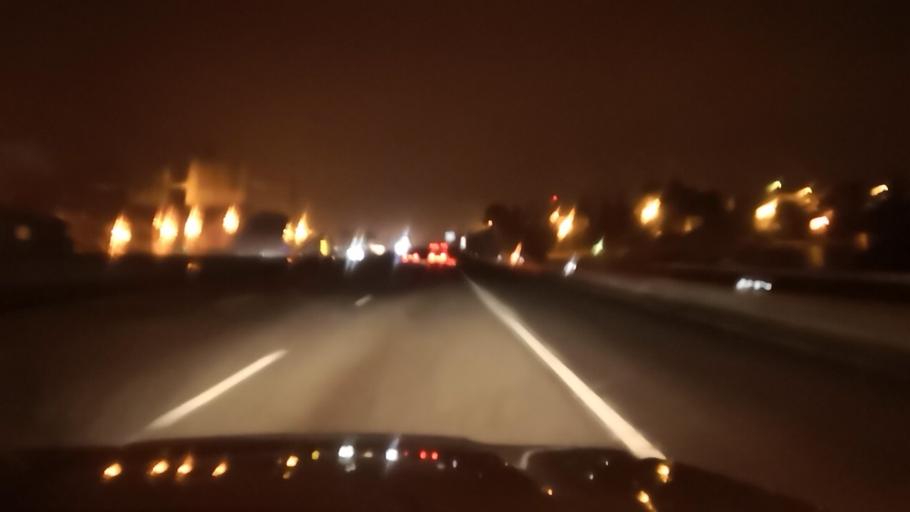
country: PT
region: Porto
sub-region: Vila Nova de Gaia
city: Perozinho
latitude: 41.0796
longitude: -8.5817
